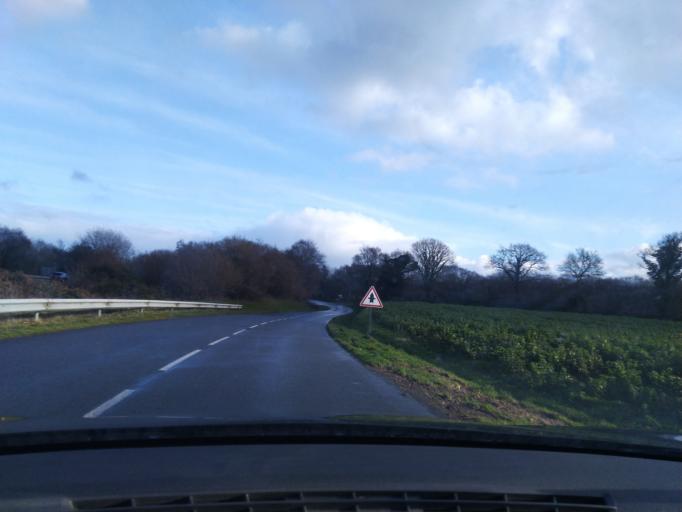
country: FR
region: Brittany
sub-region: Departement du Finistere
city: Guerlesquin
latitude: 48.5665
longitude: -3.5699
